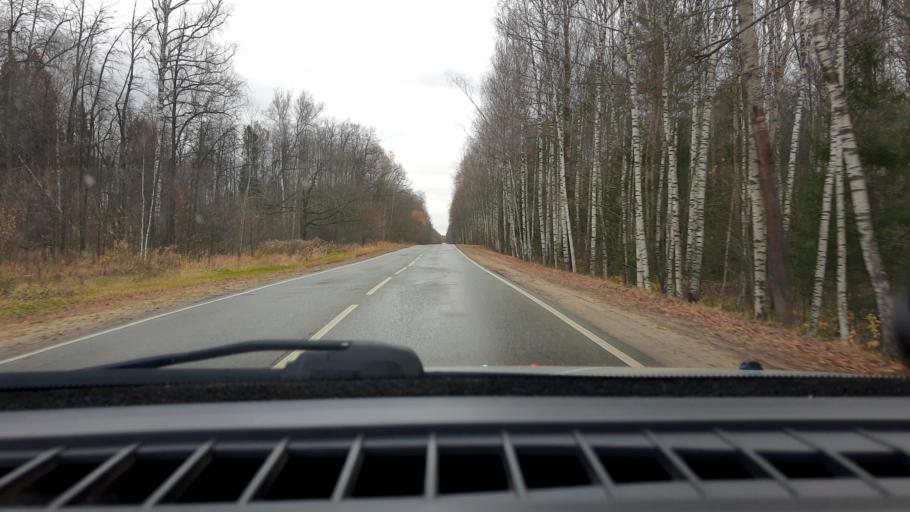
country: RU
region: Nizjnij Novgorod
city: Afonino
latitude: 56.1911
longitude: 44.0279
